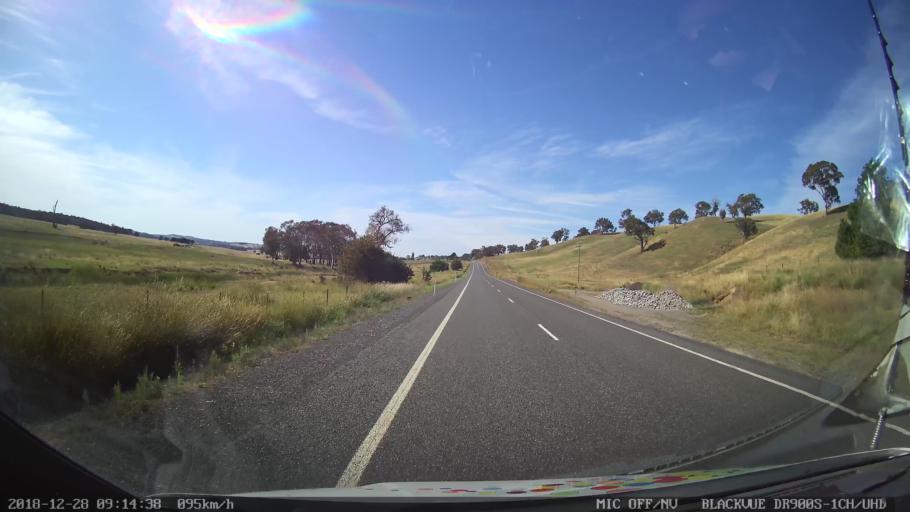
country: AU
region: New South Wales
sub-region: Upper Lachlan Shire
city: Crookwell
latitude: -34.2852
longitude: 149.3462
